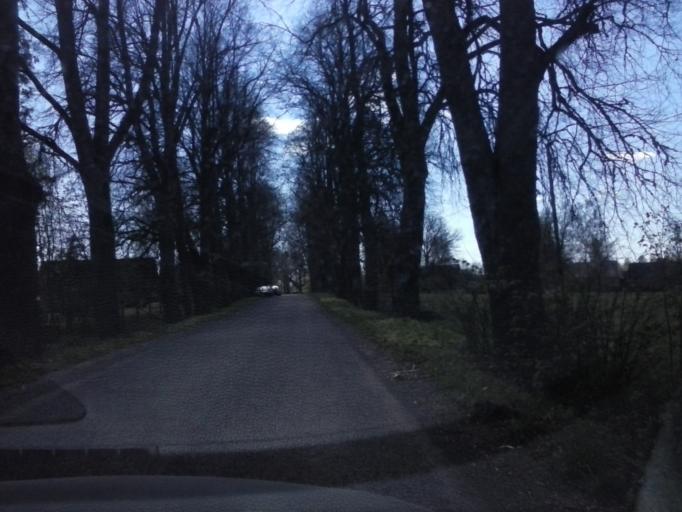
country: EE
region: Valgamaa
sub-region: Torva linn
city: Torva
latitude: 58.2293
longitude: 25.8897
